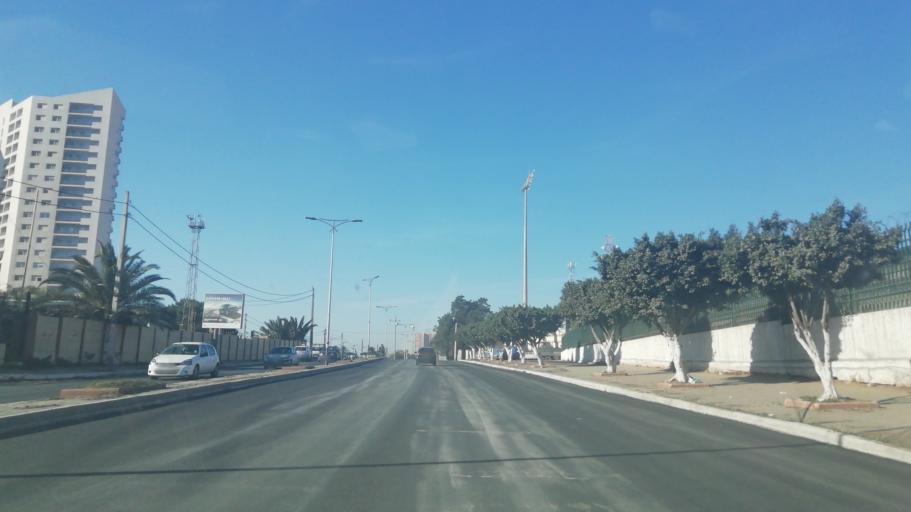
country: DZ
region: Oran
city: Oran
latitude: 35.6832
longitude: -0.6338
